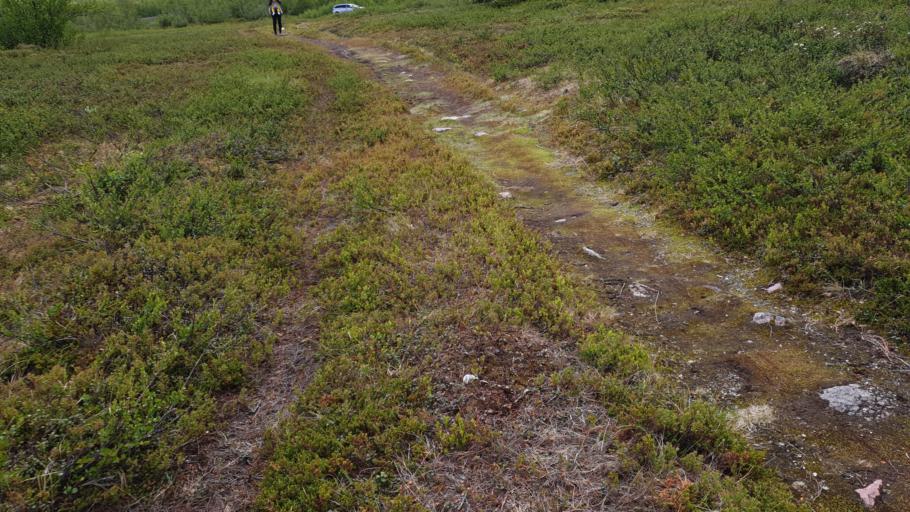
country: SE
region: Norrbotten
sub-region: Kiruna Kommun
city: Kiruna
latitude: 68.2329
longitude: 19.6196
